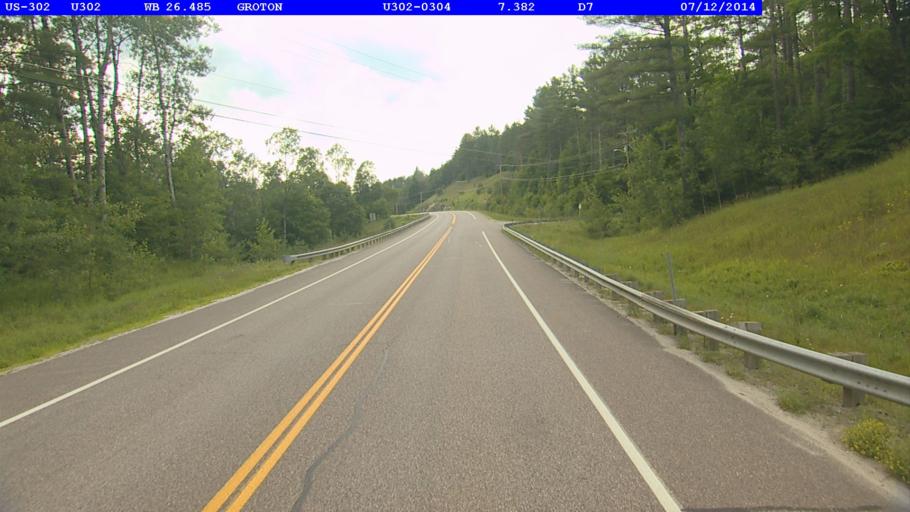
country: US
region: New Hampshire
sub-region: Grafton County
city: Woodsville
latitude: 44.2058
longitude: -72.1800
